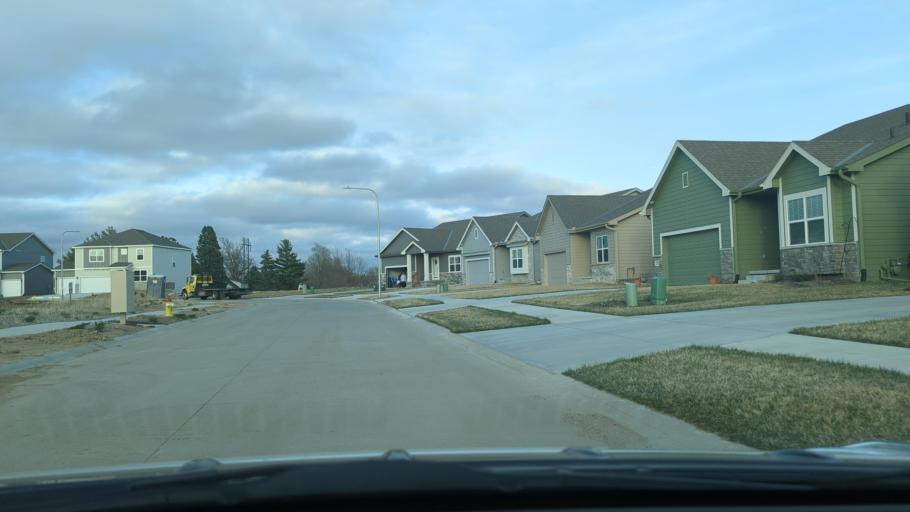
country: US
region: Nebraska
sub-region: Sarpy County
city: Offutt Air Force Base
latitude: 41.1173
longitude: -95.9792
